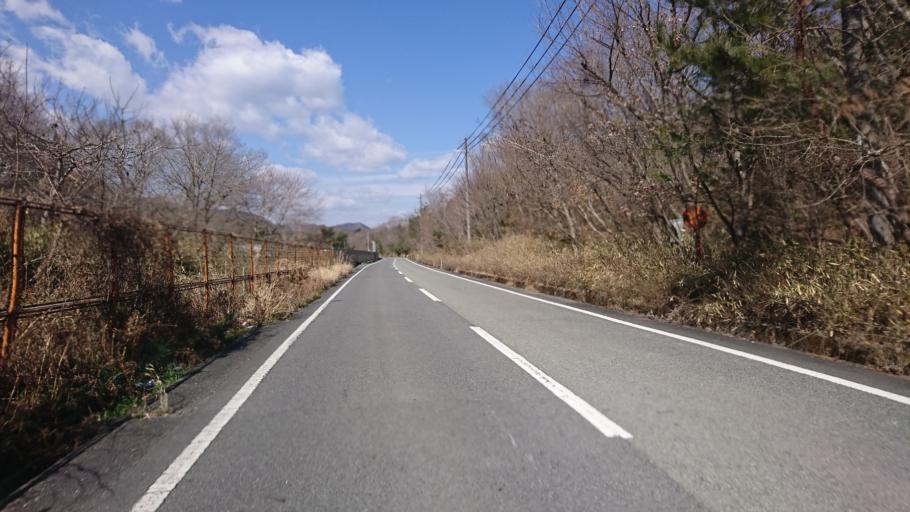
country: JP
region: Hyogo
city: Kakogawacho-honmachi
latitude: 34.8589
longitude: 134.8029
